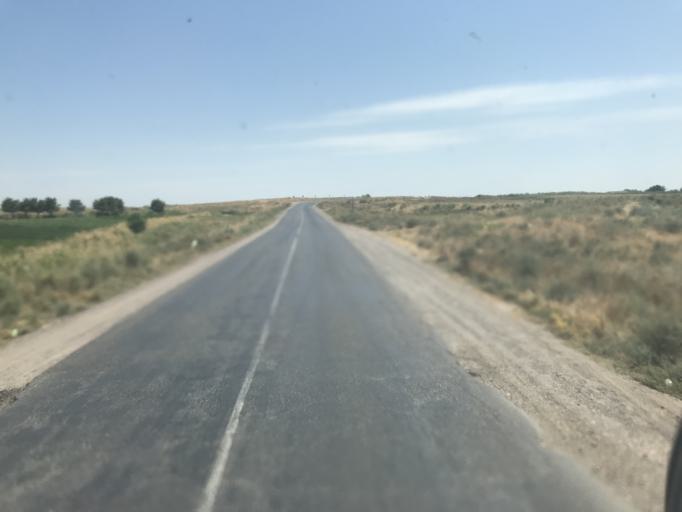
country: UZ
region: Toshkent
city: Yangiyul
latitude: 41.3472
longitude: 68.8727
